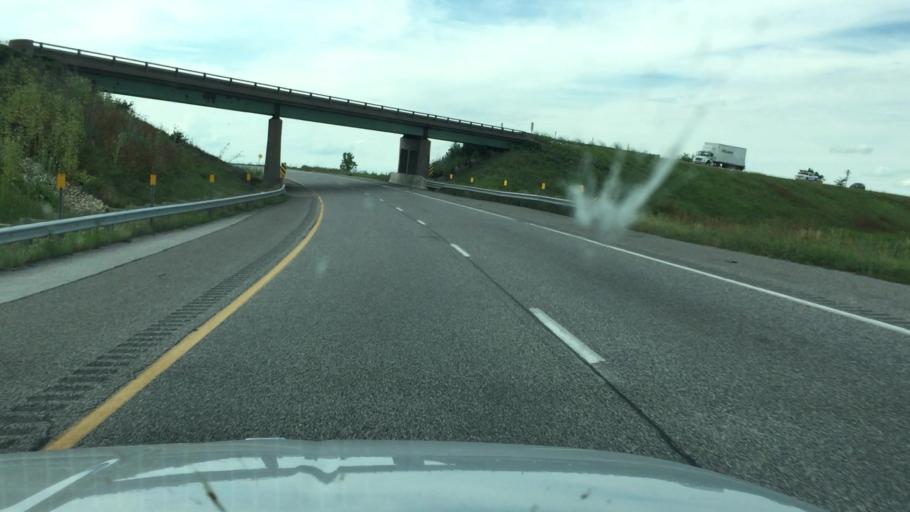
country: US
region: Iowa
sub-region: Scott County
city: Walcott
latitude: 41.6001
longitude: -90.6759
